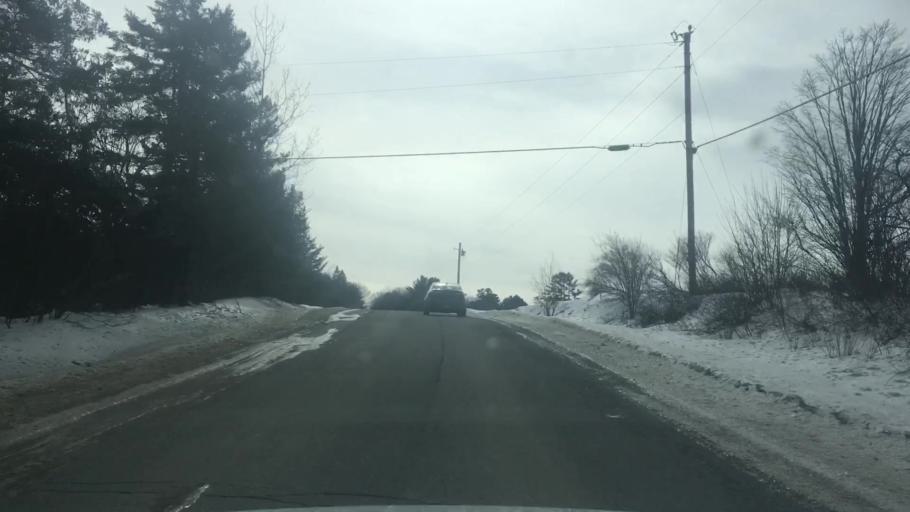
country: US
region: Maine
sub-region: Hancock County
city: Orland
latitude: 44.5928
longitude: -68.7249
